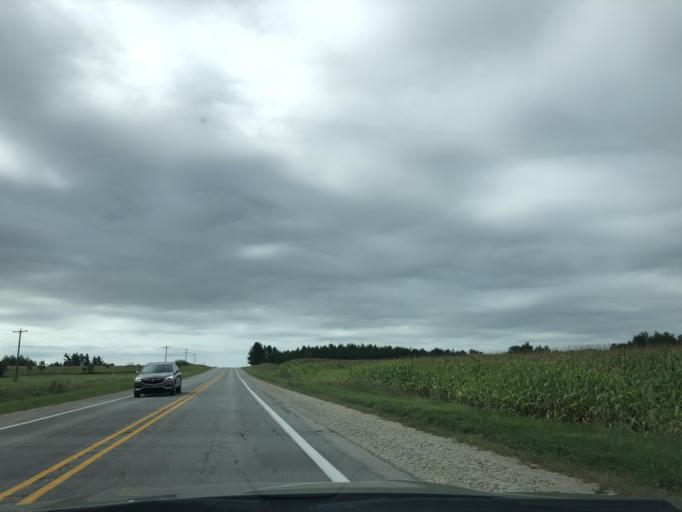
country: US
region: Michigan
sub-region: Missaukee County
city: Lake City
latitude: 44.2356
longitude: -85.2150
